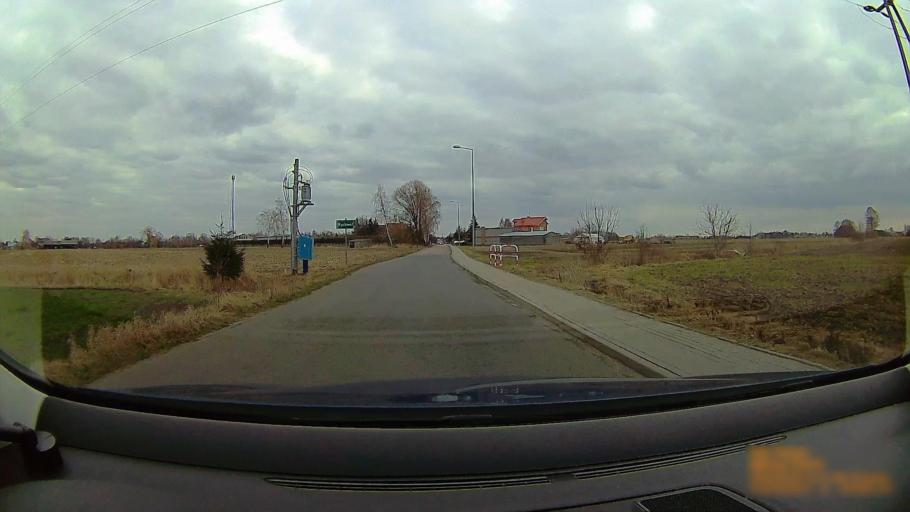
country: PL
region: Greater Poland Voivodeship
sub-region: Powiat koninski
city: Rychwal
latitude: 52.0749
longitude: 18.1512
